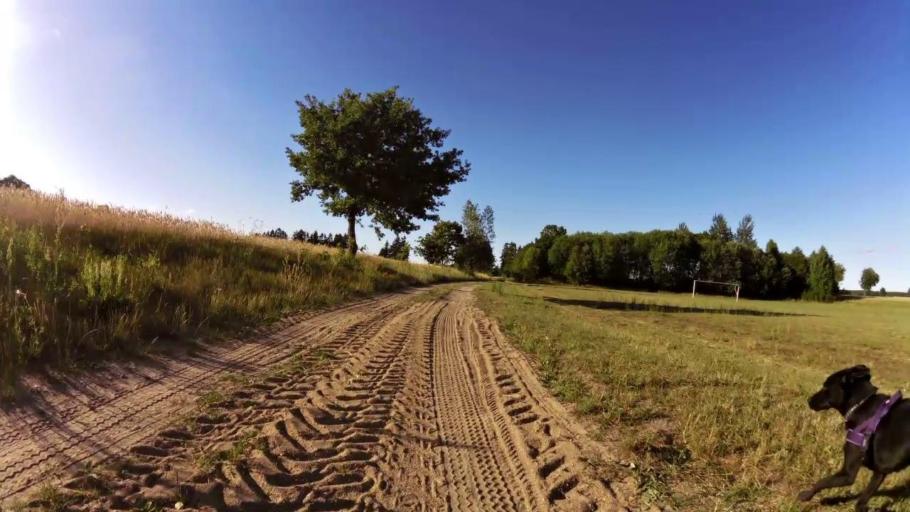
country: PL
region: West Pomeranian Voivodeship
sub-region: Powiat swidwinski
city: Swidwin
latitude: 53.7022
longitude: 15.8237
